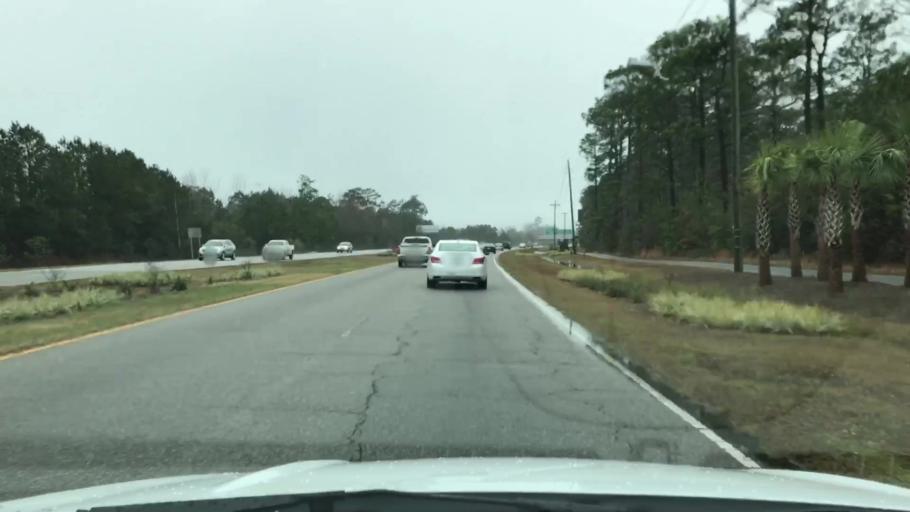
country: US
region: South Carolina
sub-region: Horry County
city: Myrtle Beach
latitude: 33.7423
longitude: -78.8428
